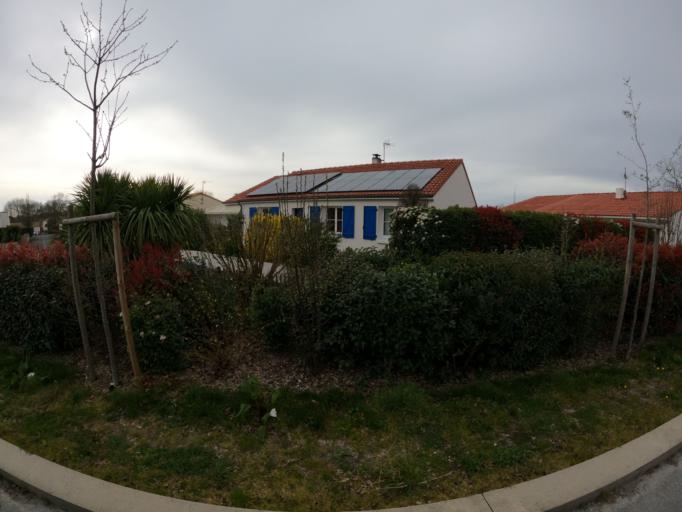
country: FR
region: Pays de la Loire
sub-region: Departement de la Vendee
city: Montaigu
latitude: 46.9836
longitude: -1.3092
